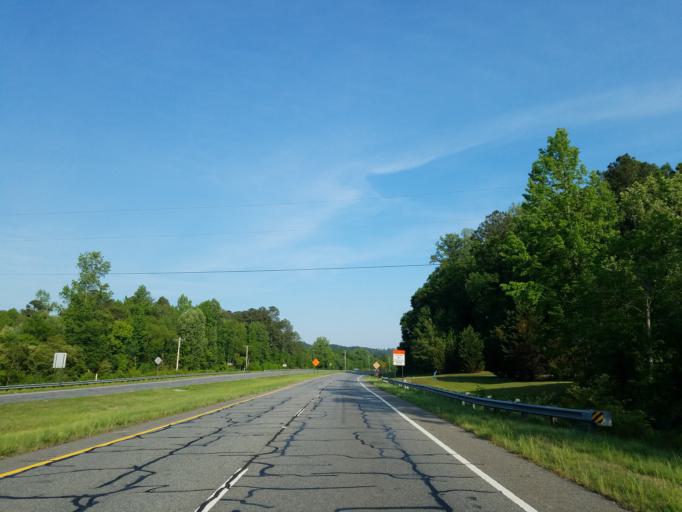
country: US
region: Georgia
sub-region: Chattooga County
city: Summerville
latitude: 34.4620
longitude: -85.2615
